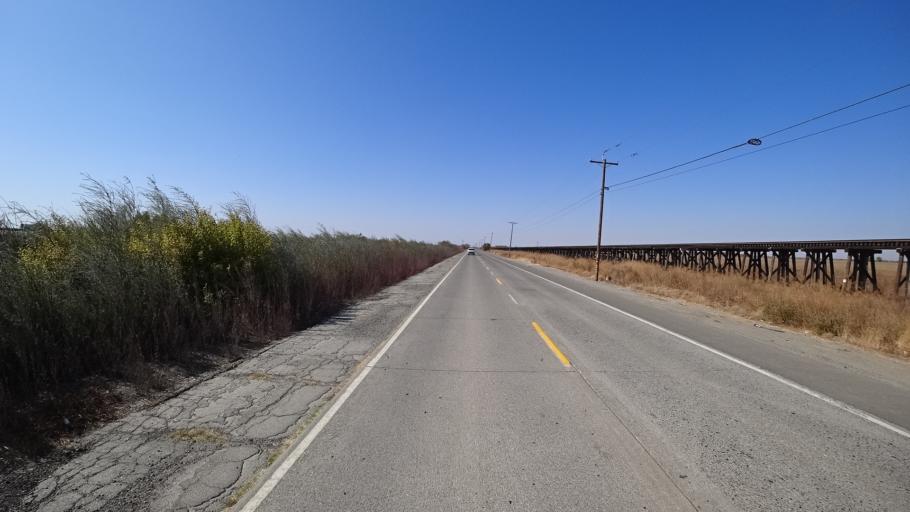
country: US
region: California
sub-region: Yolo County
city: Woodland
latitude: 38.6767
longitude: -121.6517
